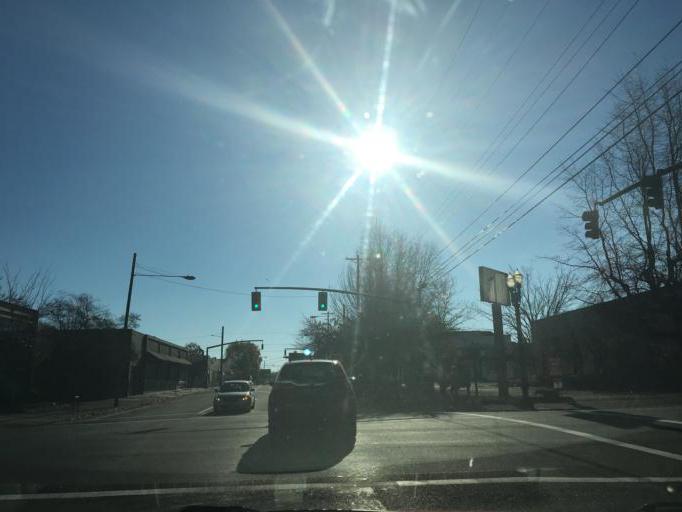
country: US
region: Oregon
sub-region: Multnomah County
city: Portland
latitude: 45.5174
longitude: -122.6587
